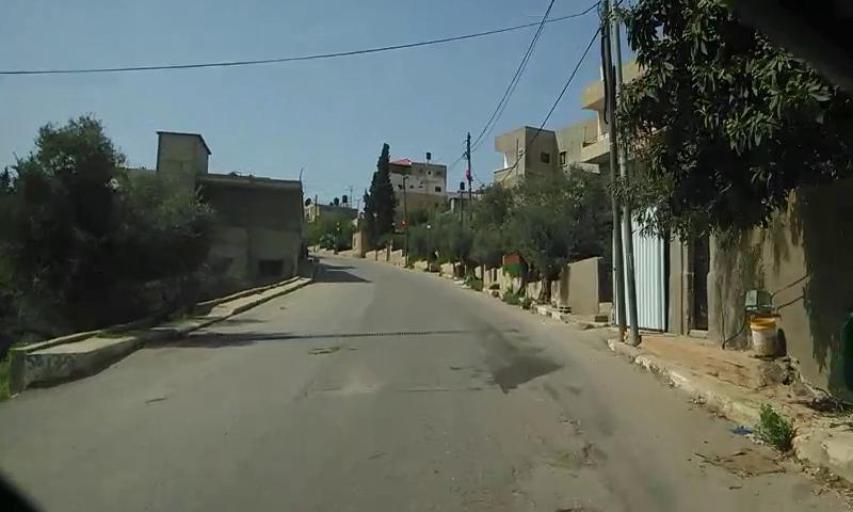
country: PS
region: West Bank
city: `Anin
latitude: 32.5011
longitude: 35.1714
